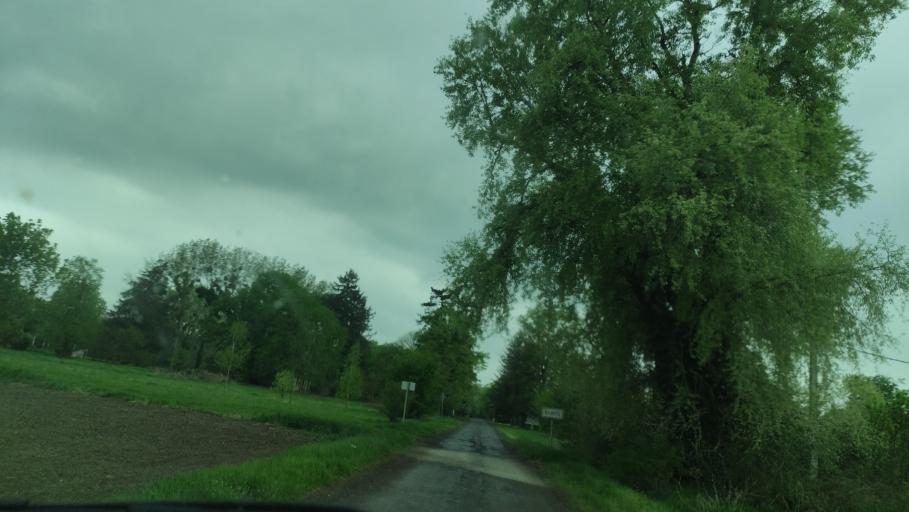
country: HR
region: Osjecko-Baranjska
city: Batina
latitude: 45.9064
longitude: 18.7635
